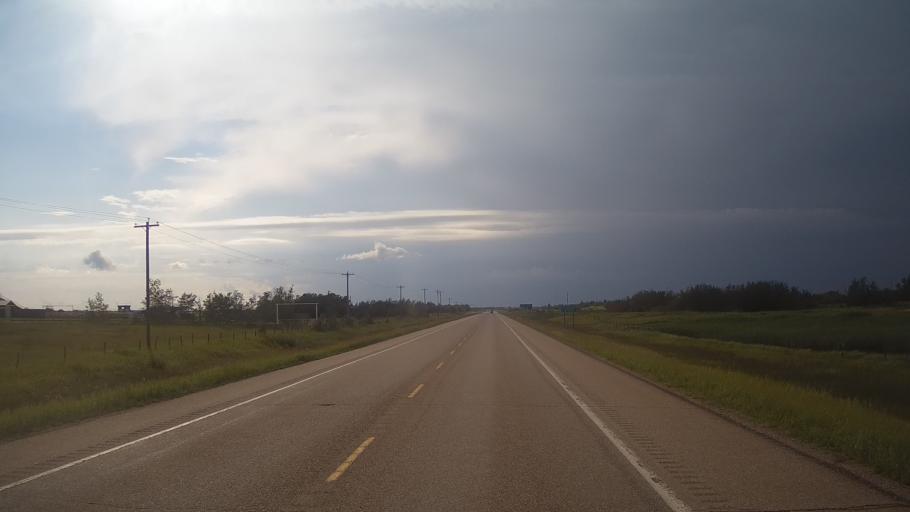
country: CA
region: Alberta
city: Viking
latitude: 53.1649
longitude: -112.0213
